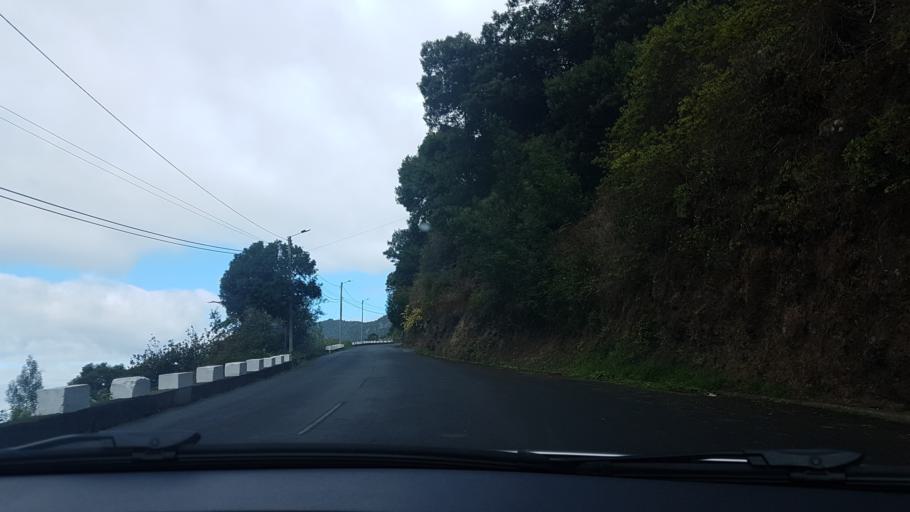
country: PT
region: Madeira
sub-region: Sao Vicente
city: Sao Vicente
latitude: 32.7797
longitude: -17.0305
